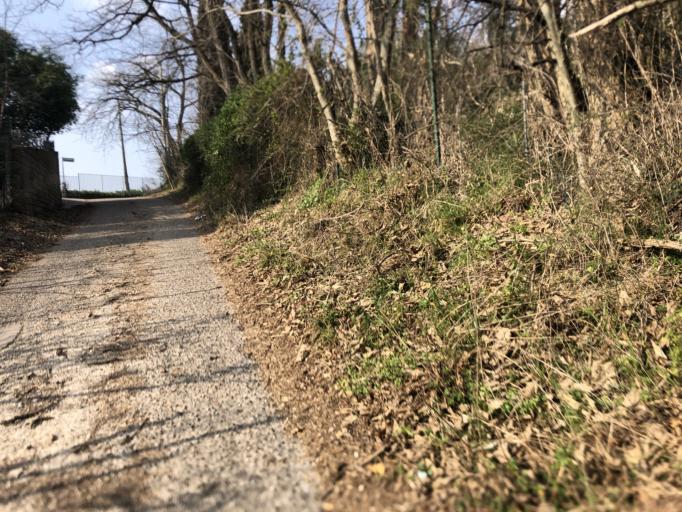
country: IT
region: Veneto
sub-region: Provincia di Verona
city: Sona
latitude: 45.4274
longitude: 10.8388
